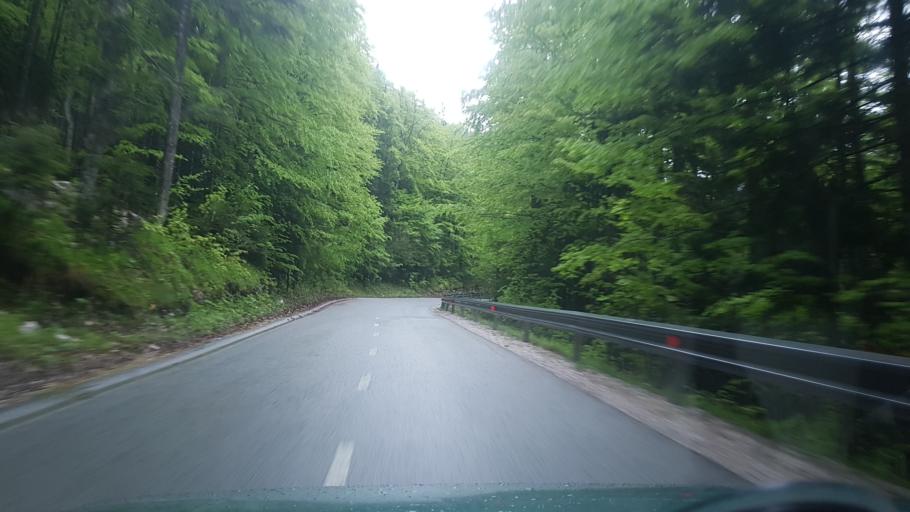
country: SI
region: Bohinj
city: Bohinjska Bistrica
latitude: 46.2567
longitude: 14.0081
